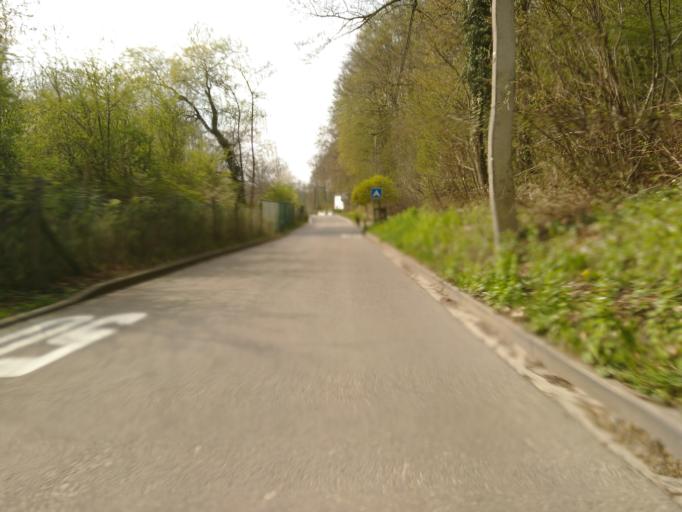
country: BE
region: Wallonia
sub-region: Province du Brabant Wallon
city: Chaumont-Gistoux
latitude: 50.6858
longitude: 4.7095
